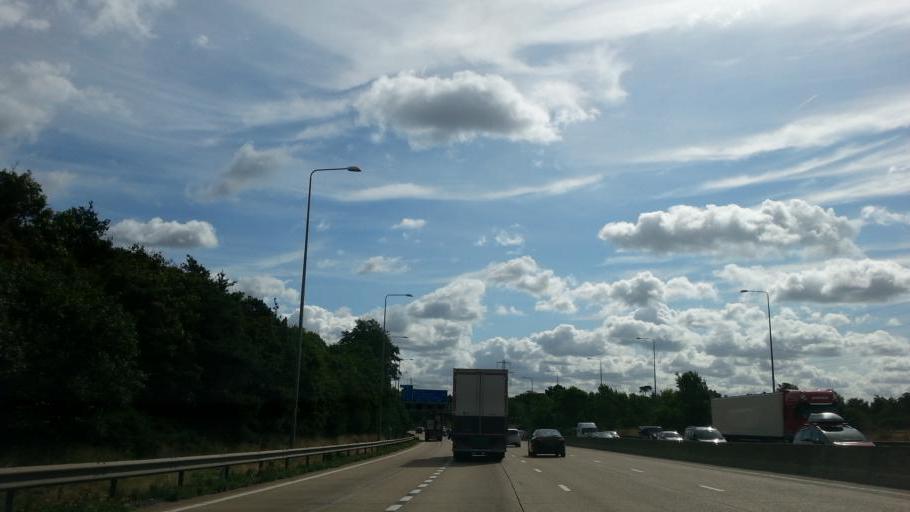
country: GB
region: England
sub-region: Hertfordshire
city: Waltham Cross
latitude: 51.6832
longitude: -0.0650
